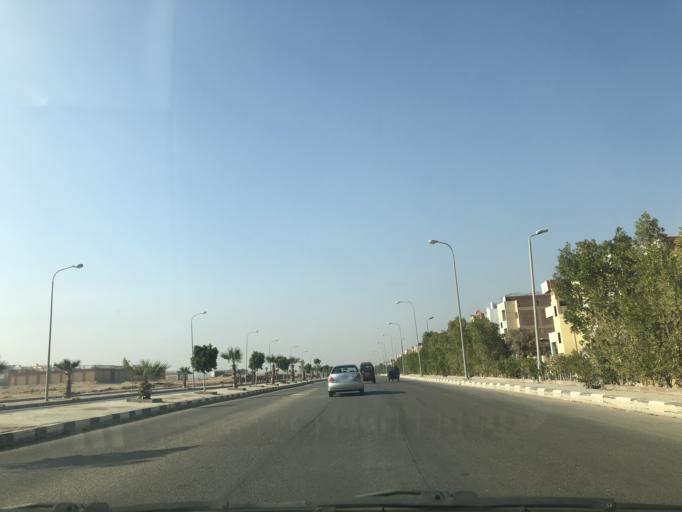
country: EG
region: Al Jizah
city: Madinat Sittah Uktubar
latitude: 29.9268
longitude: 31.0516
